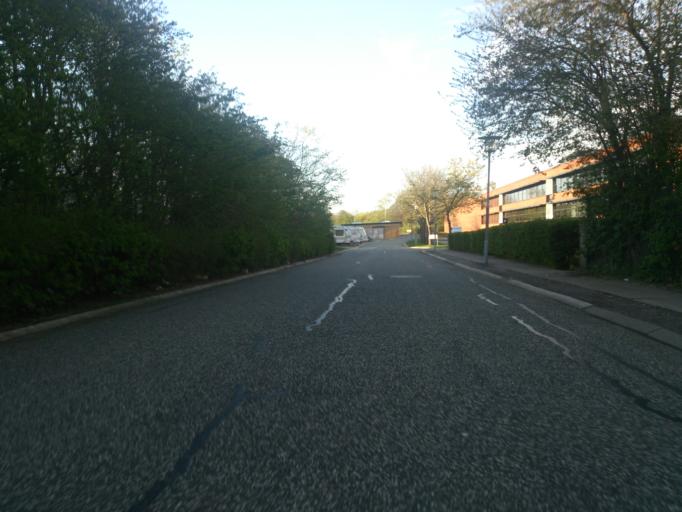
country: DK
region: Capital Region
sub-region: Ballerup Kommune
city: Ballerup
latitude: 55.7301
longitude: 12.3509
